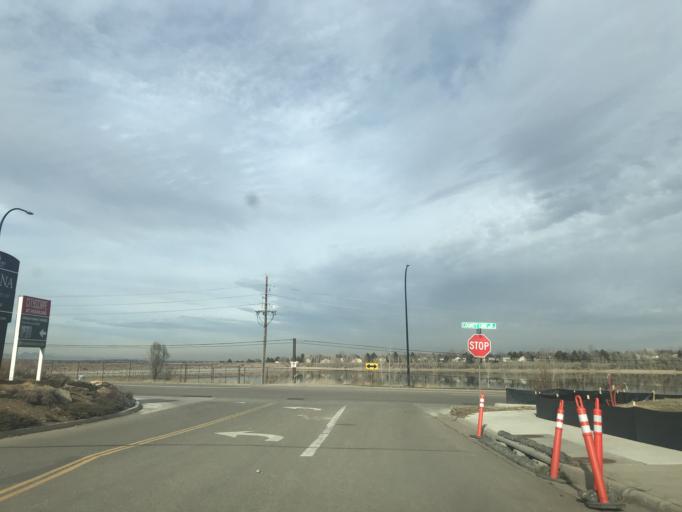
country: US
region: Colorado
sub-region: Arapahoe County
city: Columbine Valley
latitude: 39.5657
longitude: -105.0213
